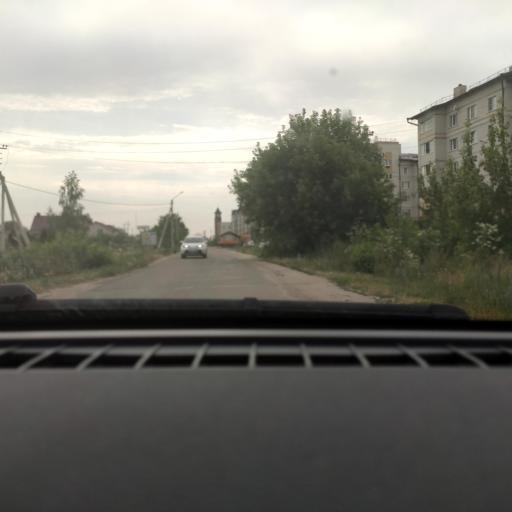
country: RU
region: Voronezj
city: Novaya Usman'
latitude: 51.6500
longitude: 39.3370
